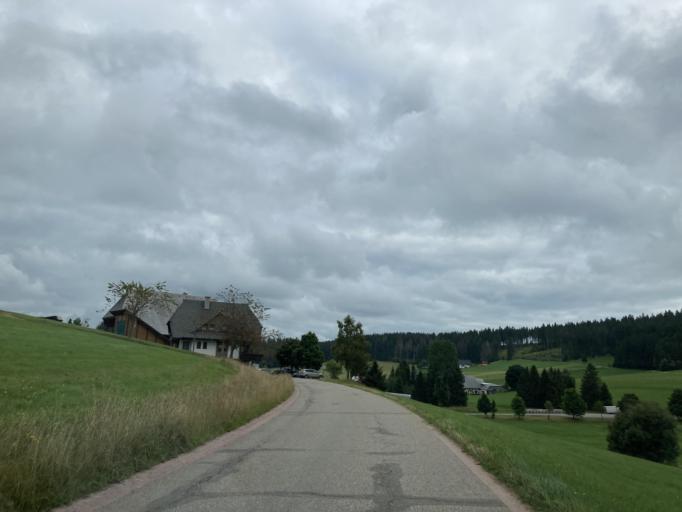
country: DE
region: Baden-Wuerttemberg
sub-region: Freiburg Region
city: Schonwald im Schwarzwald
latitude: 48.1100
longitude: 8.1846
